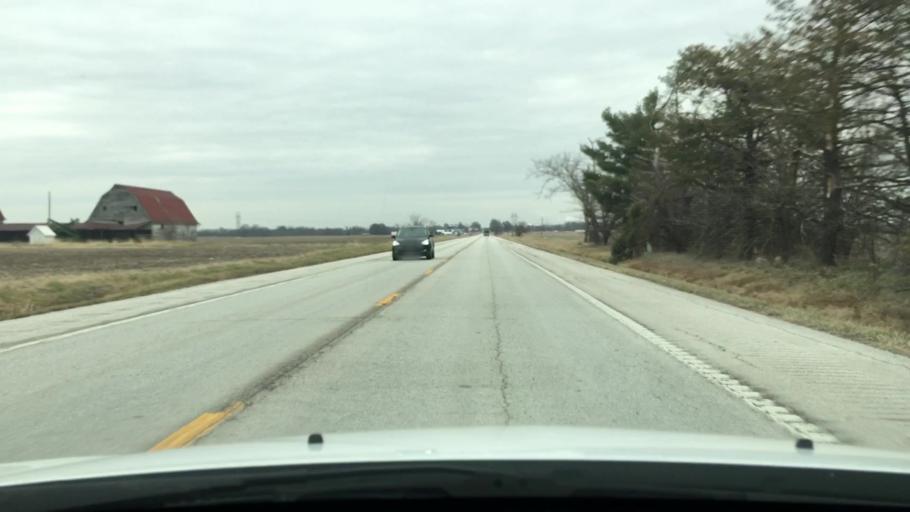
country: US
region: Missouri
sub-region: Montgomery County
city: Wellsville
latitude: 39.2210
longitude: -91.6462
